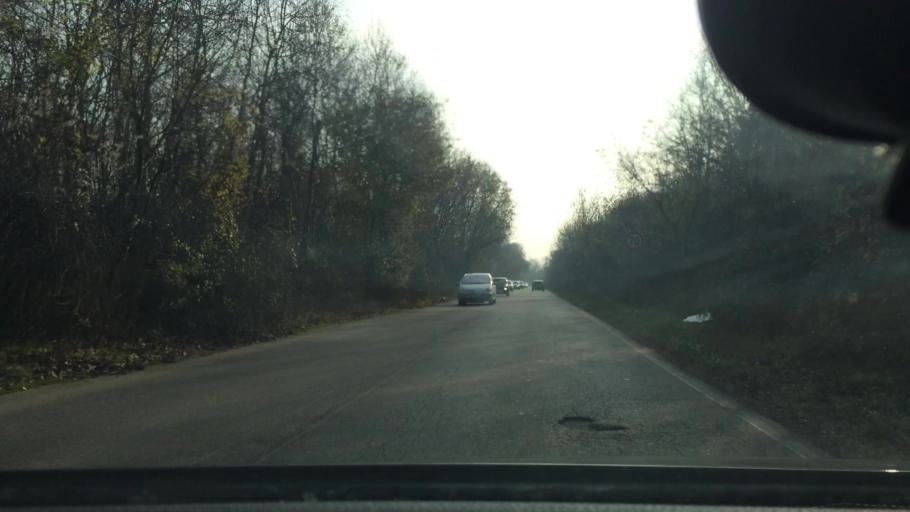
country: IT
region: Lombardy
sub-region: Provincia di Monza e Brianza
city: Villaggio del Sole
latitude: 45.6022
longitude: 9.0963
